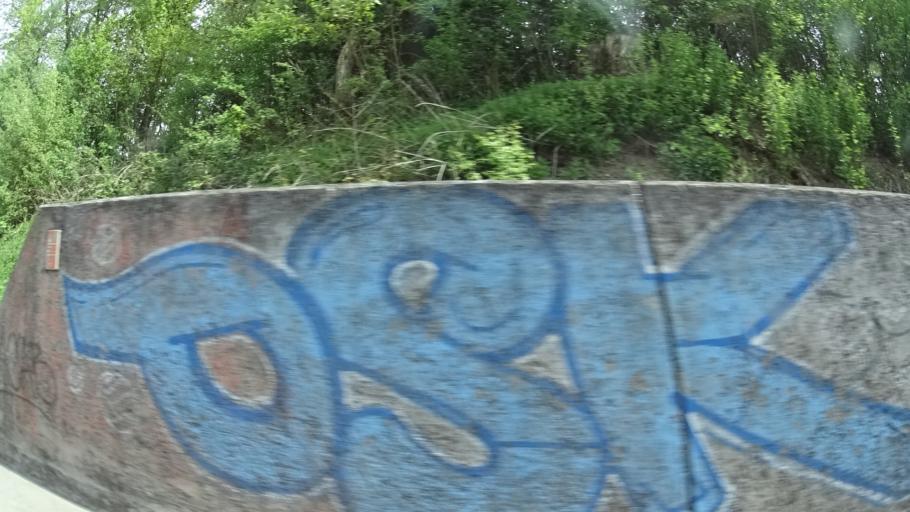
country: DE
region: Baden-Wuerttemberg
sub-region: Freiburg Region
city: Rottweil
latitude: 48.1743
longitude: 8.6307
